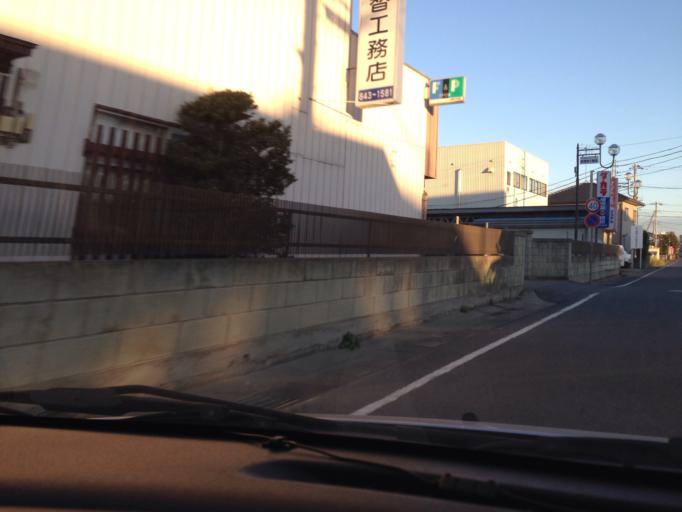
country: JP
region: Ibaraki
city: Naka
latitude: 36.0387
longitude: 140.1583
